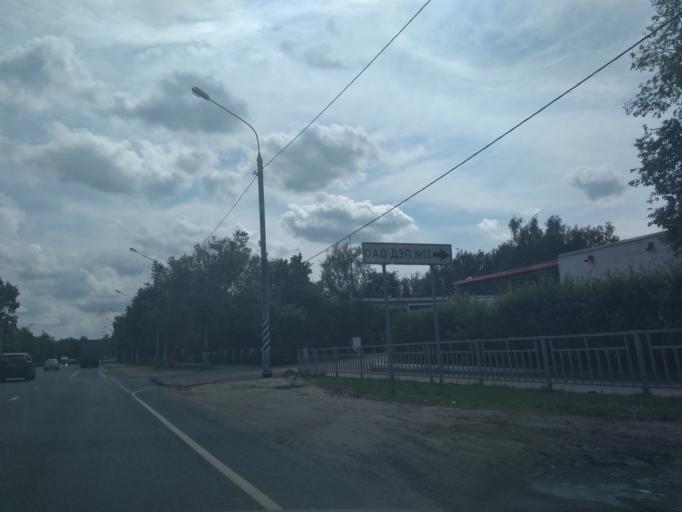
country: RU
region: Moskovskaya
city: Orekhovo-Zuyevo
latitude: 55.8226
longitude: 38.9649
